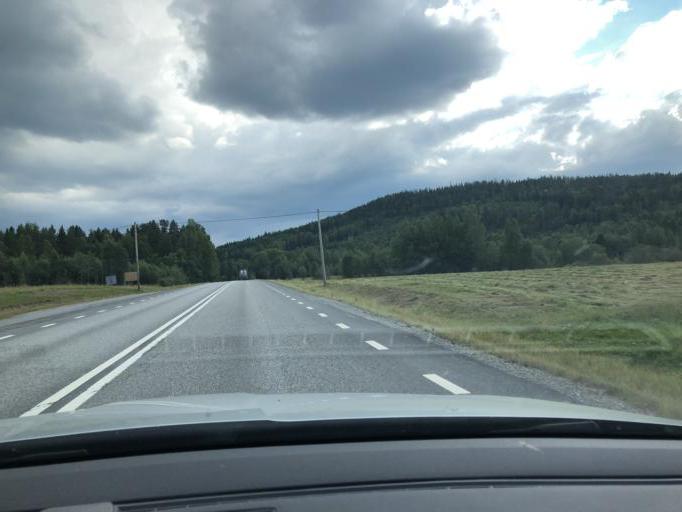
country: SE
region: Vaesternorrland
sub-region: Solleftea Kommun
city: Solleftea
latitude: 63.3104
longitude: 17.1997
